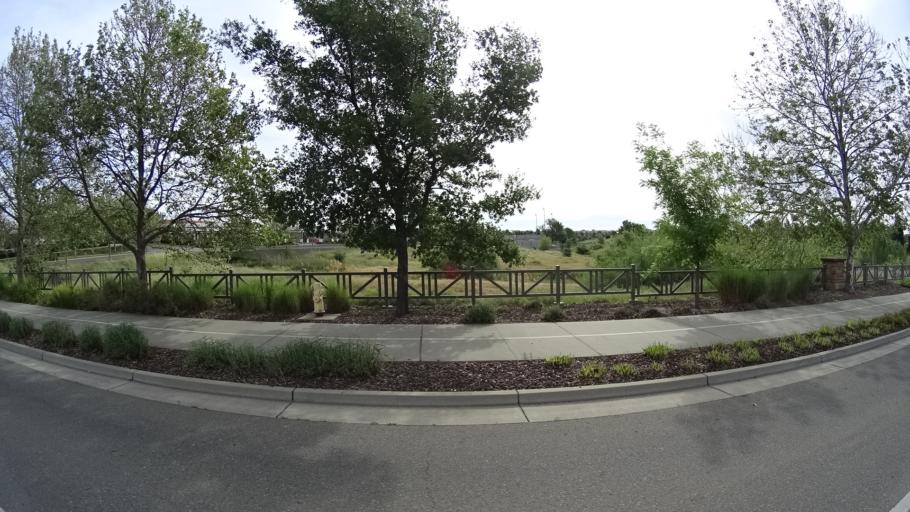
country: US
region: California
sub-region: Placer County
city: Lincoln
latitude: 38.8339
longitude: -121.2889
